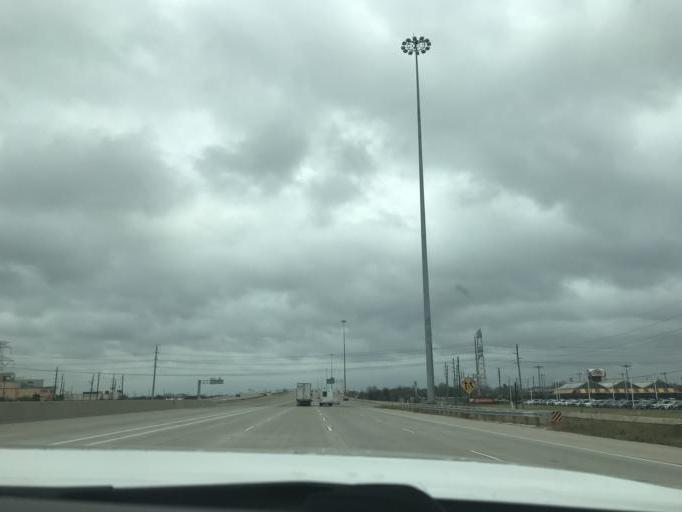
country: US
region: Texas
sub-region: Fort Bend County
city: Greatwood
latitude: 29.5601
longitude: -95.6979
